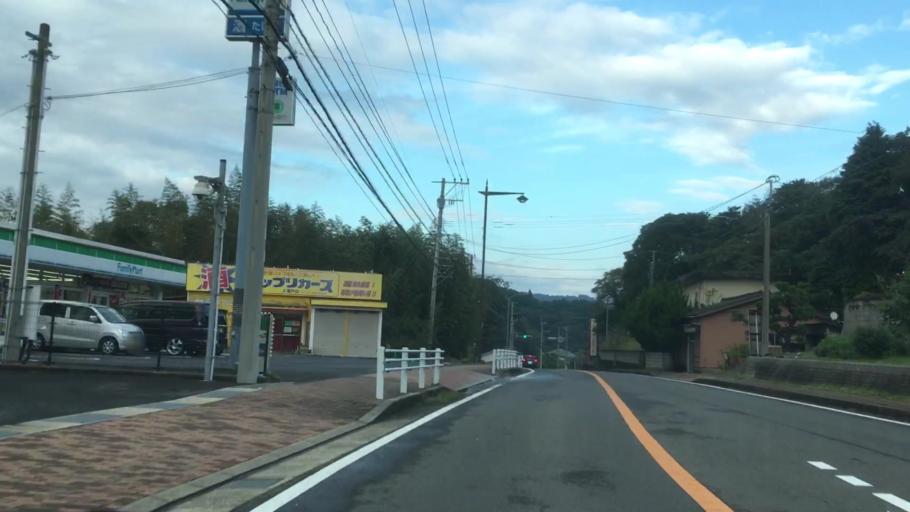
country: JP
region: Nagasaki
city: Togitsu
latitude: 32.9385
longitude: 129.6534
